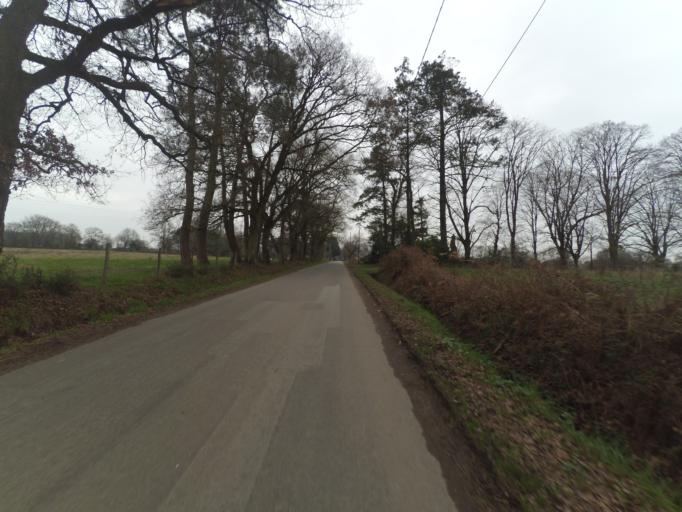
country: FR
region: Pays de la Loire
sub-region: Departement de la Loire-Atlantique
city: Sautron
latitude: 47.2568
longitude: -1.7075
